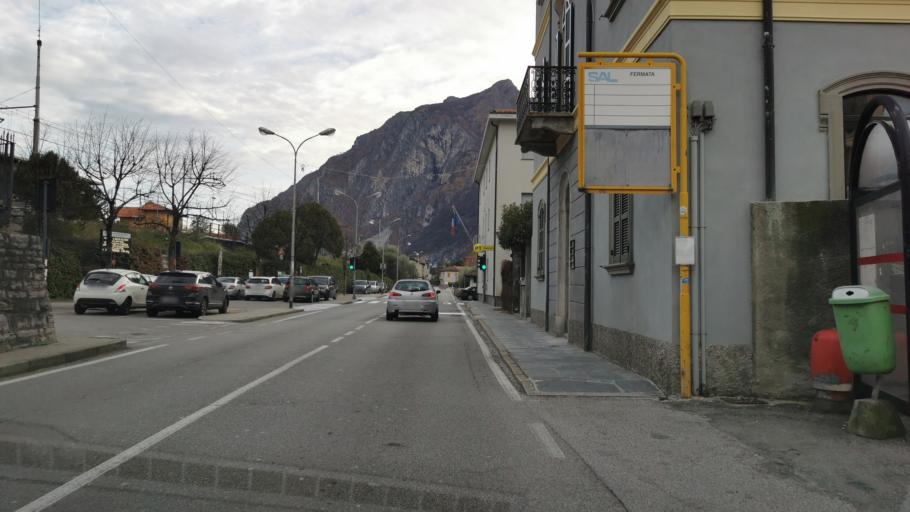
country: IT
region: Lombardy
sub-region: Provincia di Lecco
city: Abbadia Lariana
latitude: 45.8997
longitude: 9.3321
